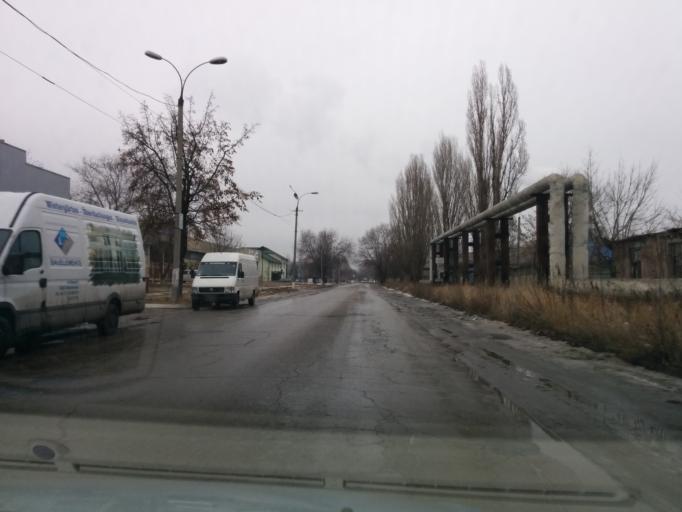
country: MD
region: Chisinau
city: Vatra
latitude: 47.0447
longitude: 28.7981
